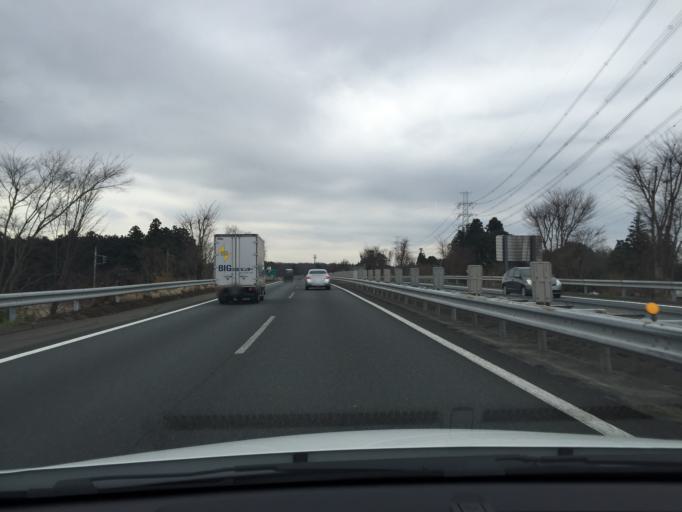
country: JP
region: Saitama
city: Sakado
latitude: 35.9110
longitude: 139.3877
